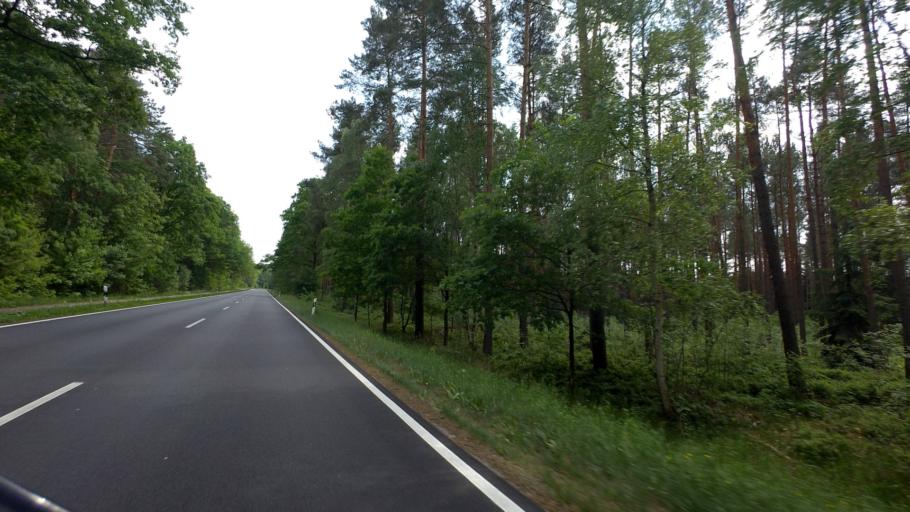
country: DE
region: Saxony
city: Niesky
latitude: 51.3316
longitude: 14.8145
